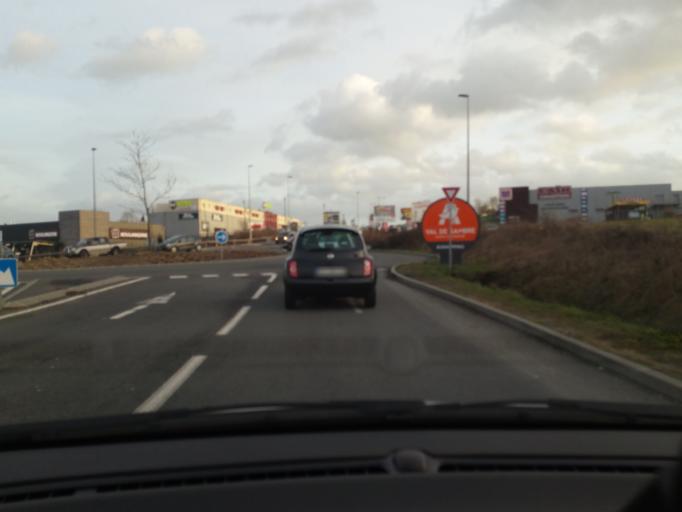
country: FR
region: Nord-Pas-de-Calais
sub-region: Departement du Nord
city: Hautmont
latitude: 50.2524
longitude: 3.9401
